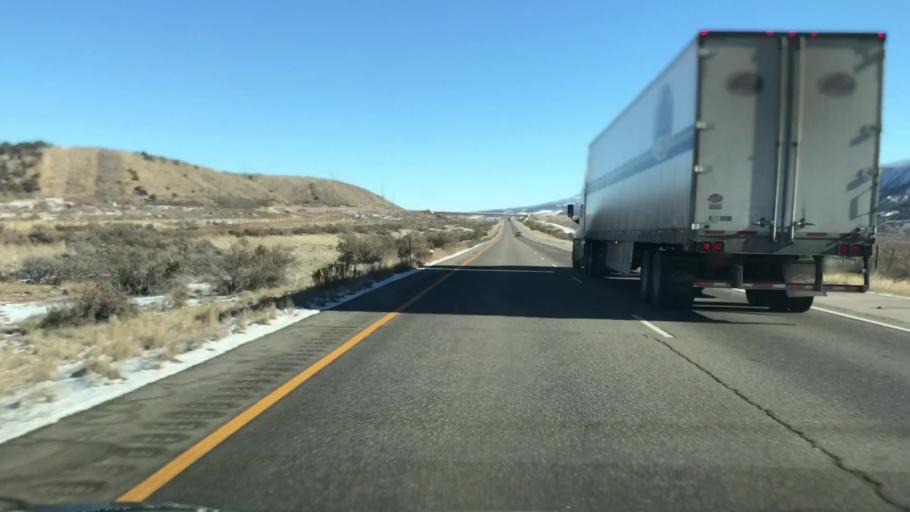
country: US
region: Colorado
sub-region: Garfield County
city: Battlement Mesa
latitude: 39.4758
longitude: -107.9999
